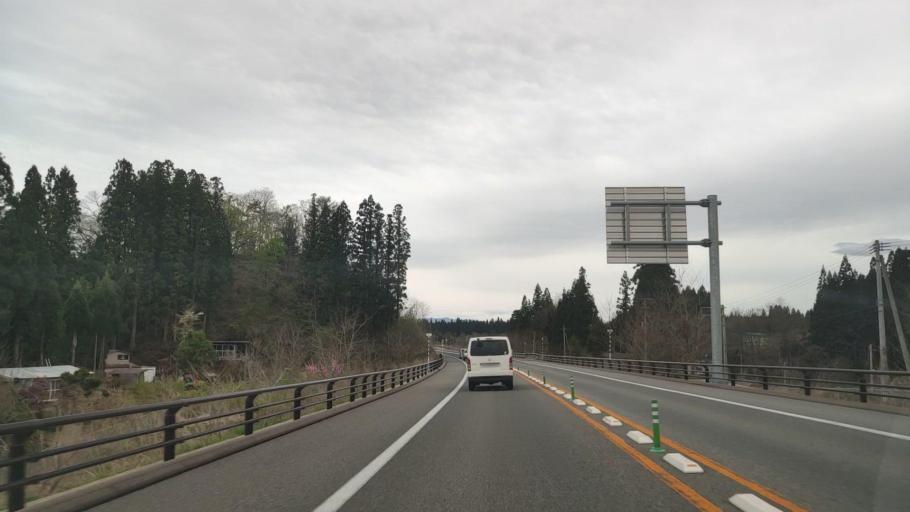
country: JP
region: Akita
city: Odate
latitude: 40.3154
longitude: 140.5818
